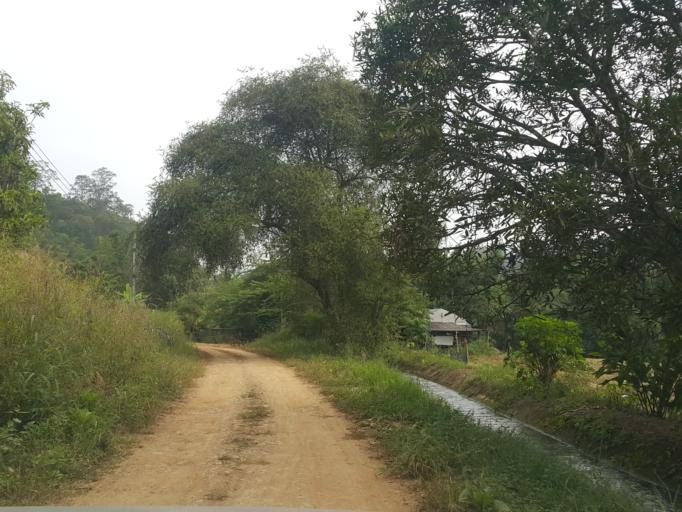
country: TH
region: Mae Hong Son
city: Wiang Nuea
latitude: 19.3885
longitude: 98.4671
